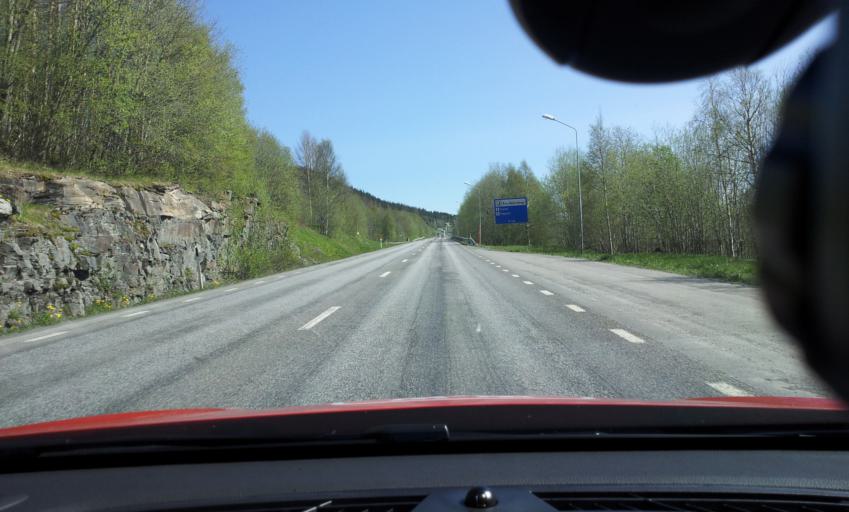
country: SE
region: Jaemtland
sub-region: Are Kommun
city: Are
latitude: 63.3840
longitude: 13.1332
